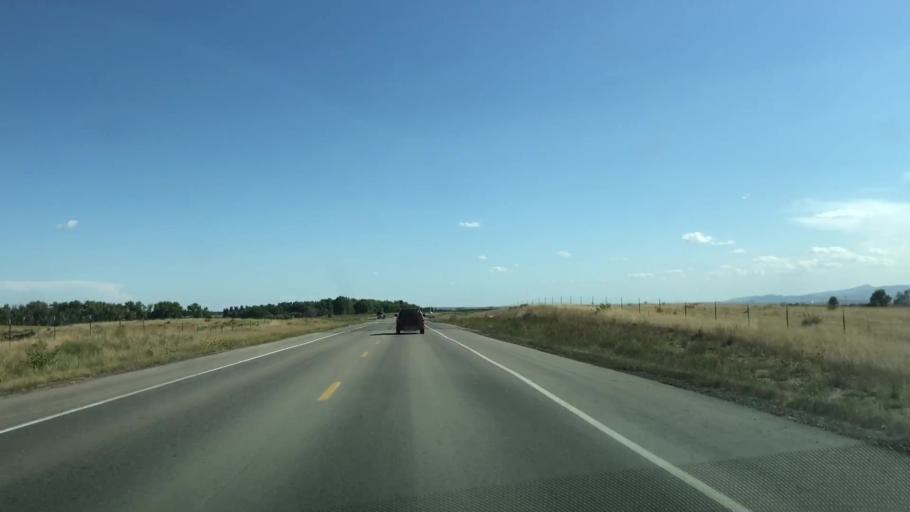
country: US
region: Colorado
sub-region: Larimer County
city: Wellington
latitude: 40.7683
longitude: -105.1200
